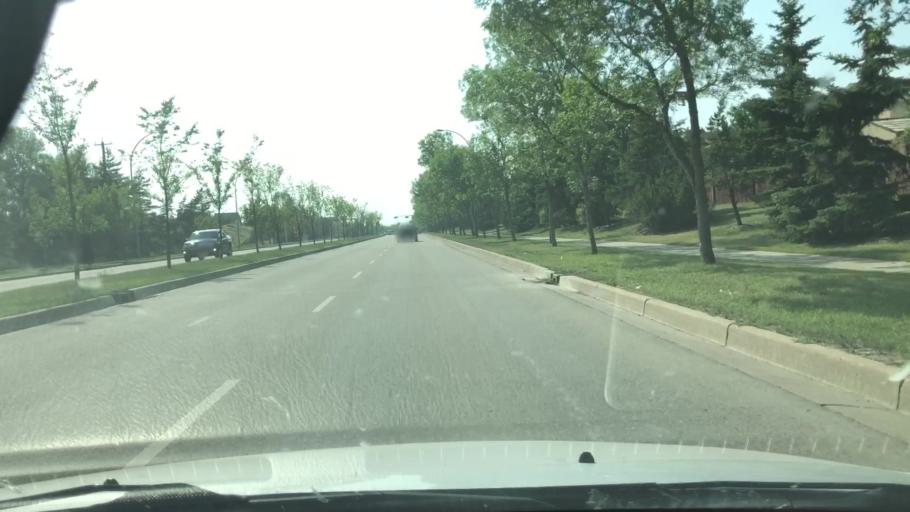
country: CA
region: Alberta
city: Edmonton
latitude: 53.6142
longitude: -113.5042
